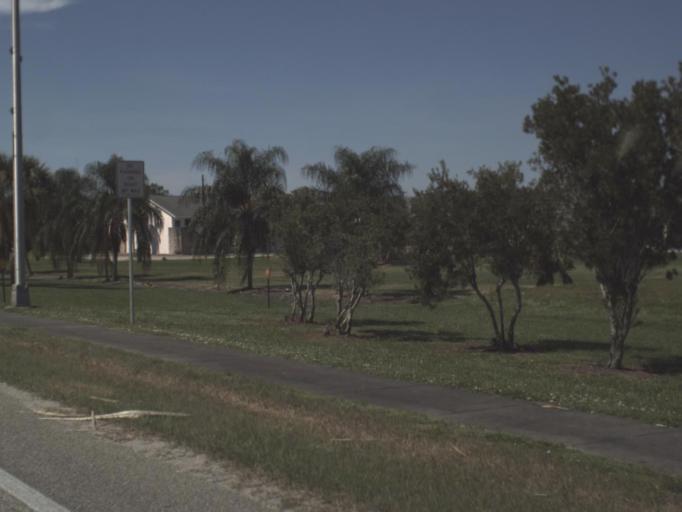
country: US
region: Florida
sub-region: Glades County
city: Moore Haven
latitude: 26.8339
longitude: -81.1050
